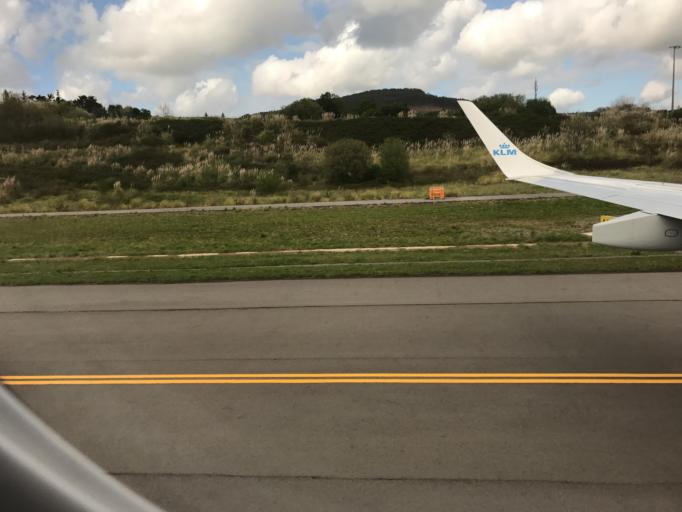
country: ES
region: Basque Country
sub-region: Bizkaia
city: Sondika
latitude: 43.3037
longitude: -2.9124
